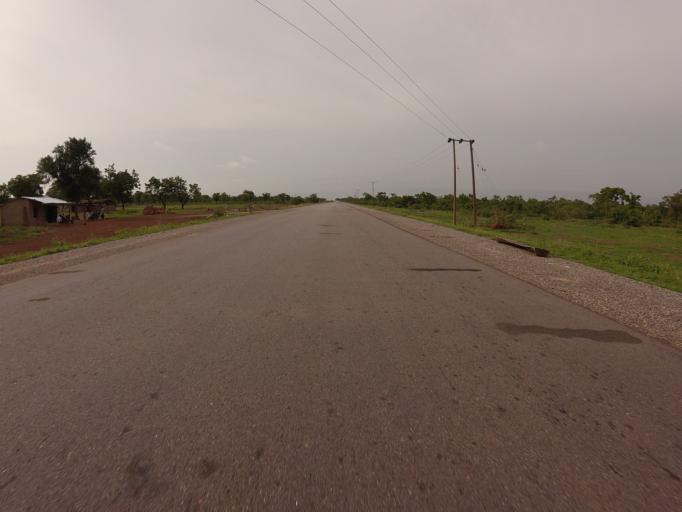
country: GH
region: Northern
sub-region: Yendi
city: Yendi
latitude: 9.6234
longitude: -0.0533
